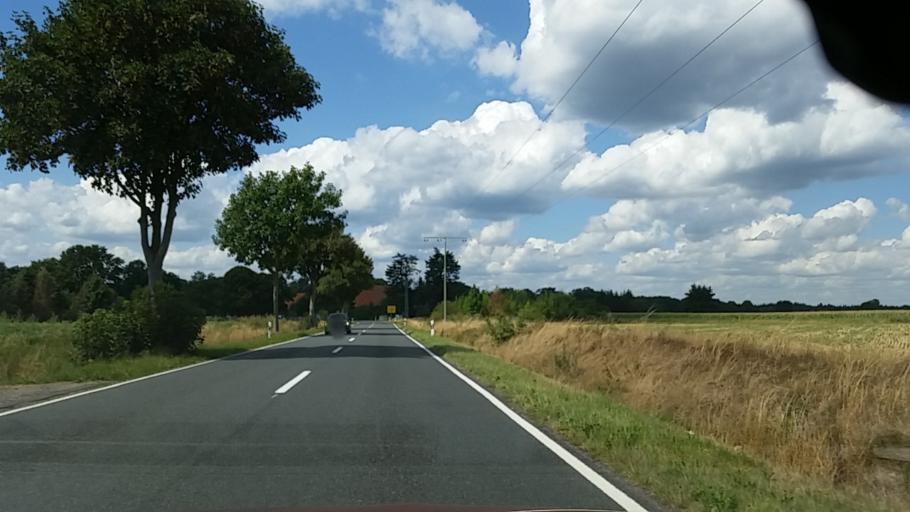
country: DE
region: Lower Saxony
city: Sprakensehl
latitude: 52.7638
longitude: 10.4981
